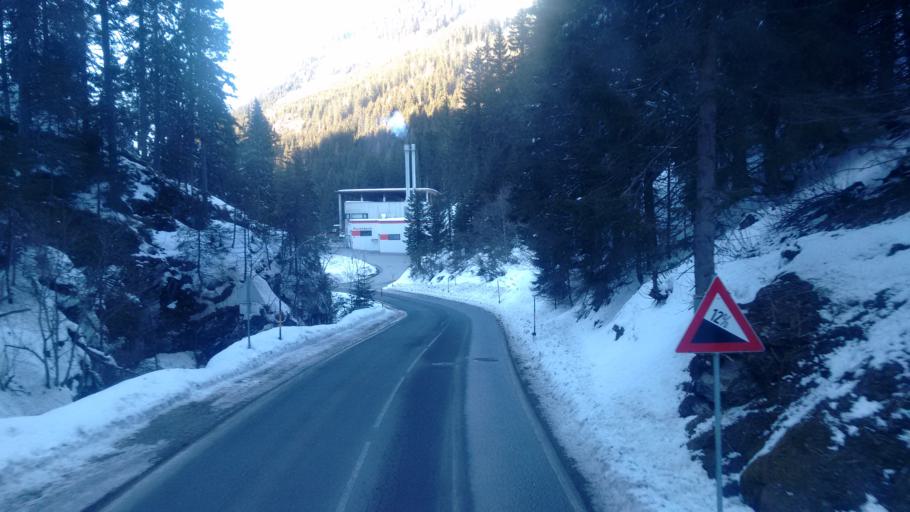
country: AT
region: Salzburg
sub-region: Politischer Bezirk Sankt Johann im Pongau
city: Untertauern
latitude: 47.2992
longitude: 13.4569
